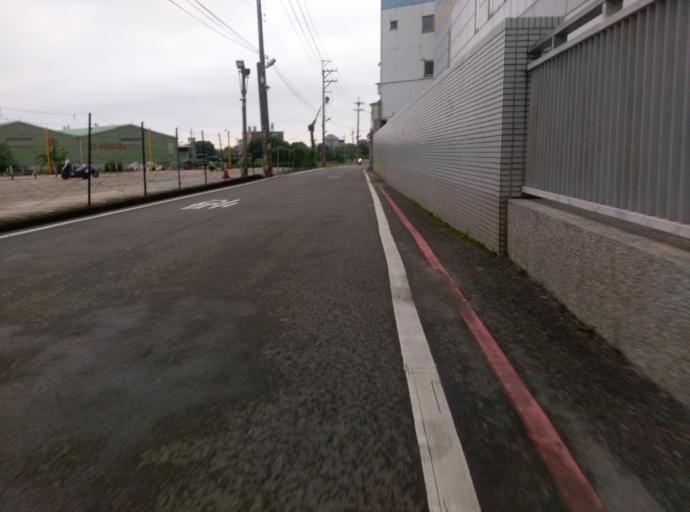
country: TW
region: Taiwan
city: Daxi
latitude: 24.9083
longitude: 121.2418
